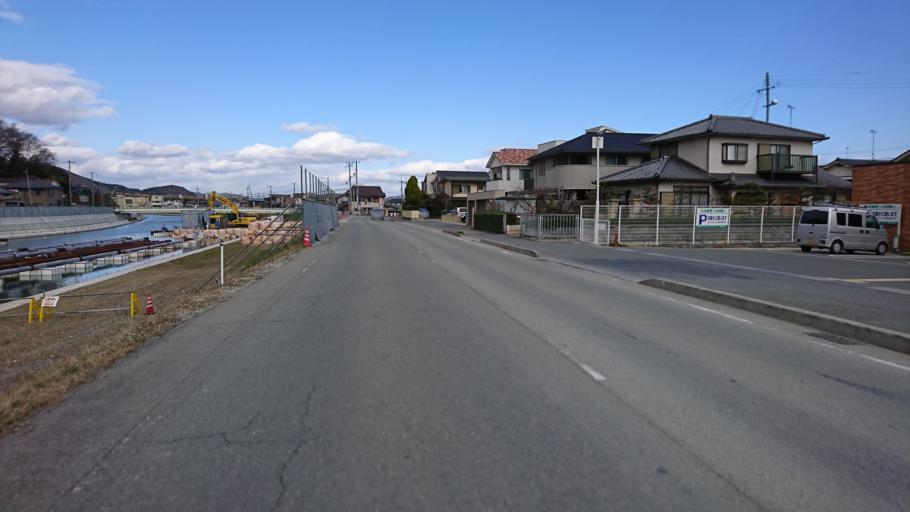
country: JP
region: Hyogo
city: Kakogawacho-honmachi
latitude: 34.7746
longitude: 134.7996
